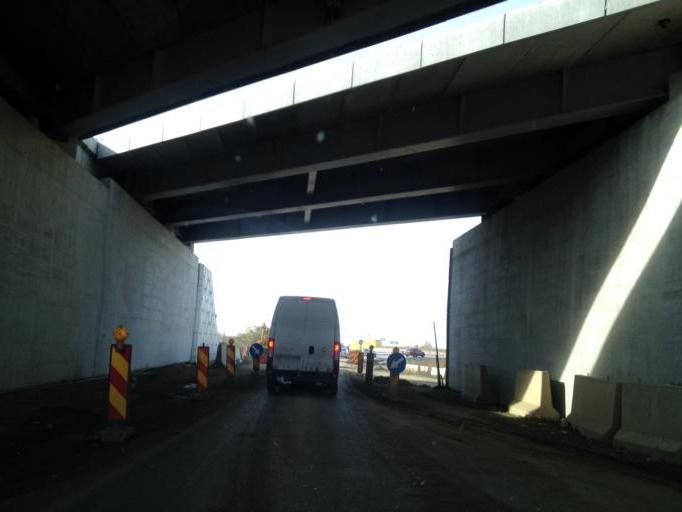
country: RO
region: Timis
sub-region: Comuna Margina
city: Margina
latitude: 45.8580
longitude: 22.2443
